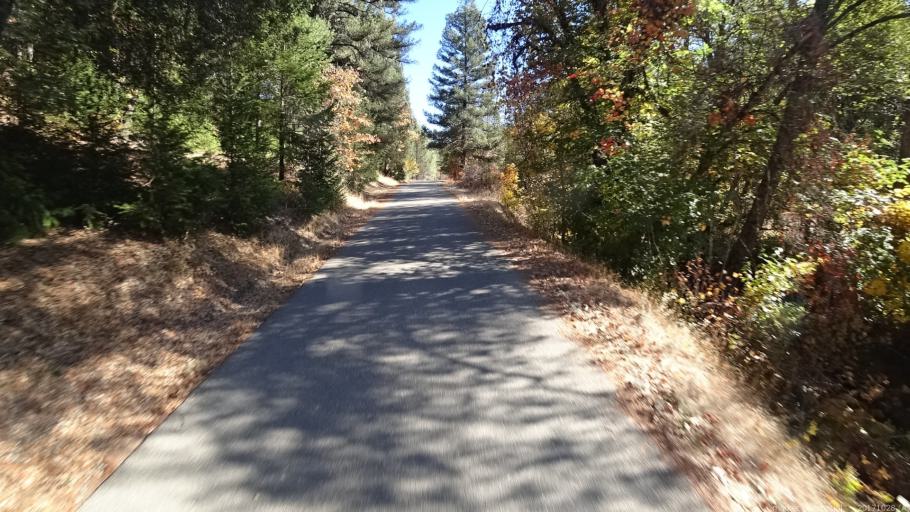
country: US
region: California
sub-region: Shasta County
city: Shasta
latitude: 40.7627
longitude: -122.5668
